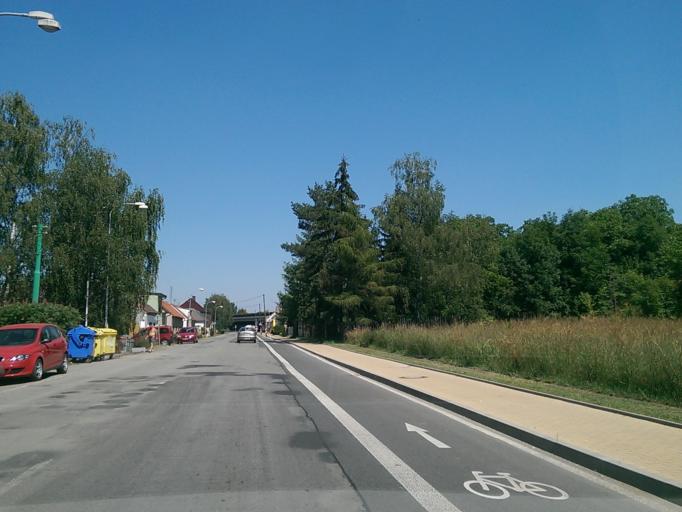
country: CZ
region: Central Bohemia
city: Benatky nad Jizerou
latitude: 50.2904
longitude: 14.8413
